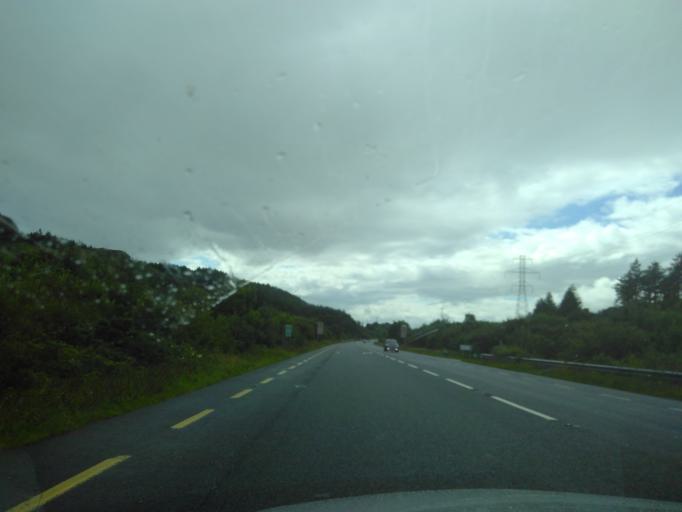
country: IE
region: Ulster
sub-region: County Donegal
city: Donegal
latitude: 54.7053
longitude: -7.9787
